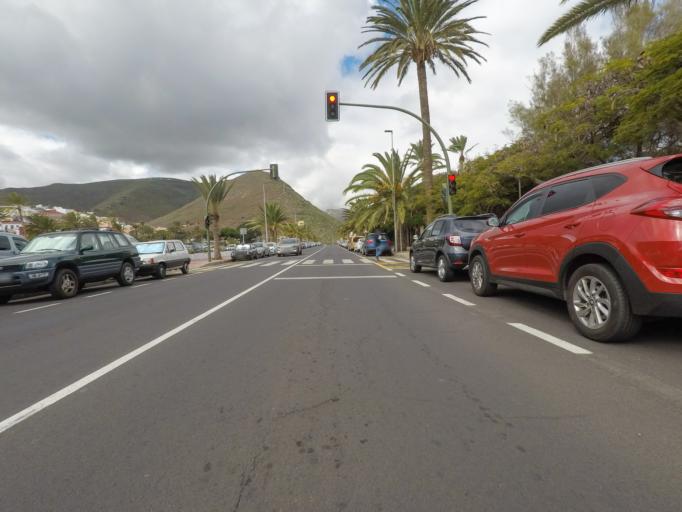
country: ES
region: Canary Islands
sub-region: Provincia de Santa Cruz de Tenerife
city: San Sebastian de la Gomera
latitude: 28.0900
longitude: -17.1119
